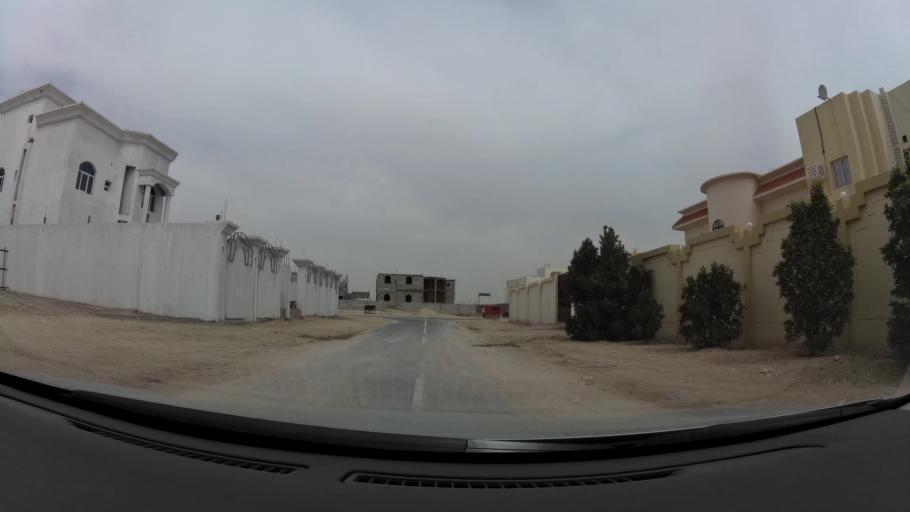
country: QA
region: Baladiyat ar Rayyan
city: Ar Rayyan
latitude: 25.2131
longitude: 51.4472
